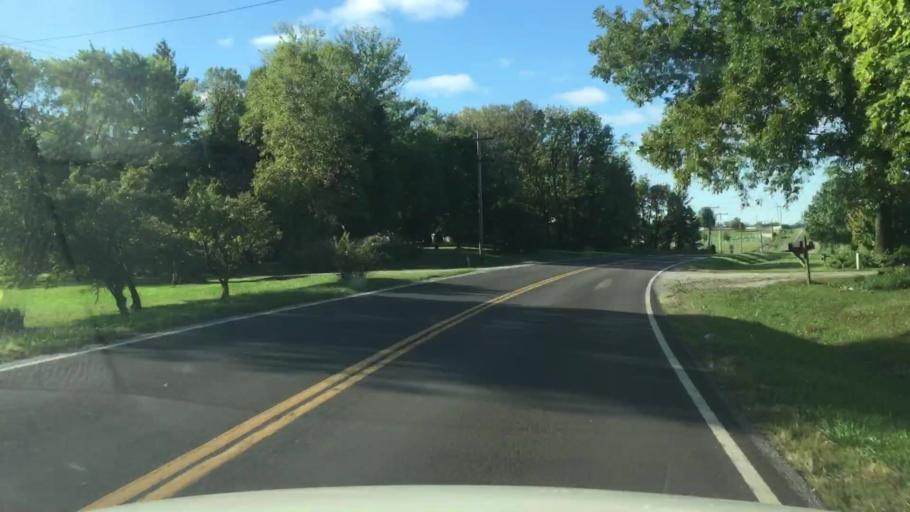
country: US
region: Missouri
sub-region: Howard County
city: New Franklin
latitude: 39.0333
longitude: -92.7435
